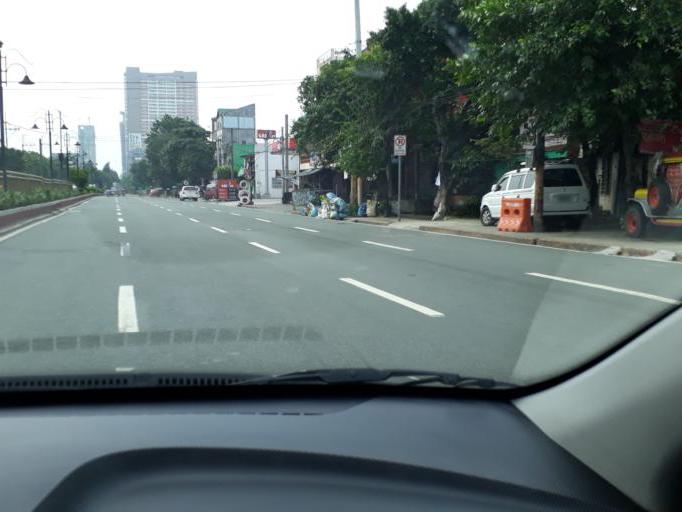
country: PH
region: Metro Manila
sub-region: City of Manila
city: Quiapo
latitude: 14.6053
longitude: 120.9969
